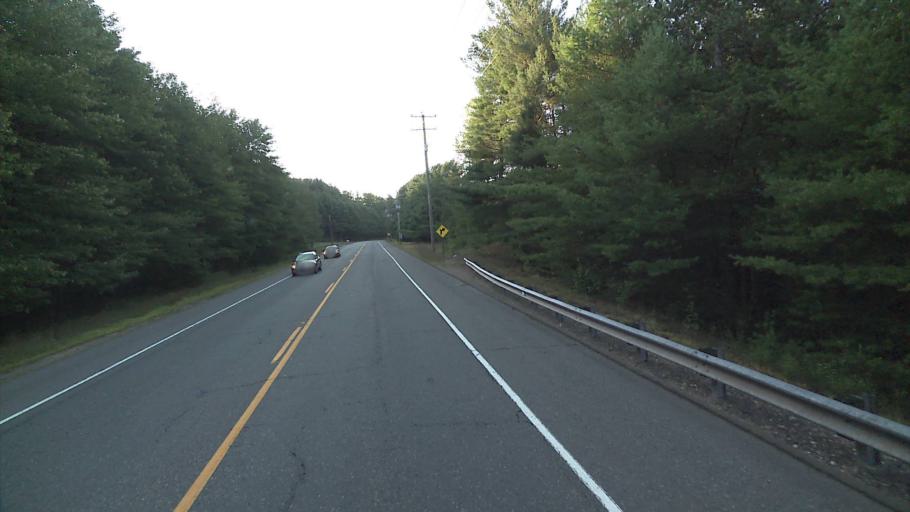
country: US
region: Connecticut
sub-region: Tolland County
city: Stafford Springs
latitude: 41.9081
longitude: -72.2908
